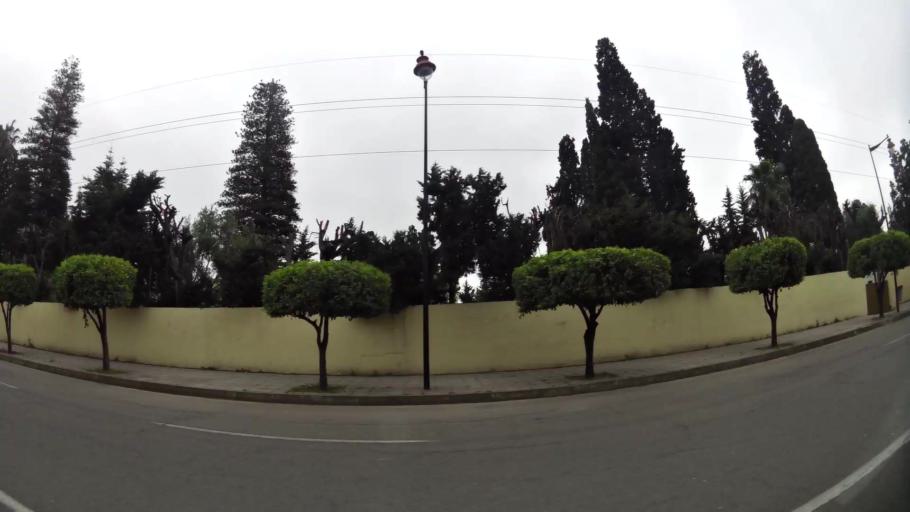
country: MA
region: Fes-Boulemane
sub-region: Fes
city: Fes
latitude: 34.0499
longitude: -4.9987
